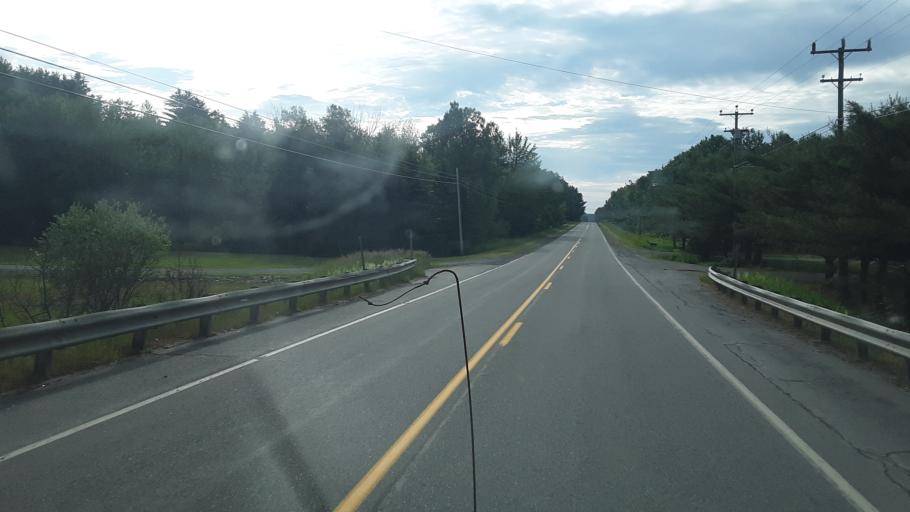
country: US
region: Maine
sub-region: Penobscot County
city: Medway
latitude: 45.5977
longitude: -68.5036
